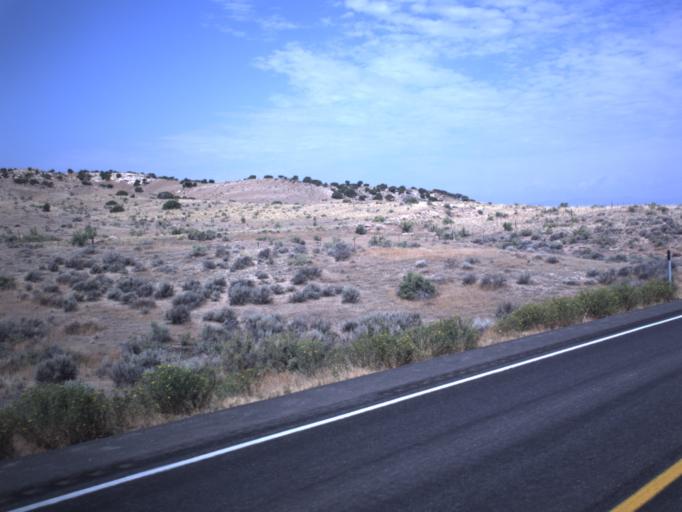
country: US
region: Utah
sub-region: Uintah County
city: Naples
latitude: 40.3519
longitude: -109.3084
